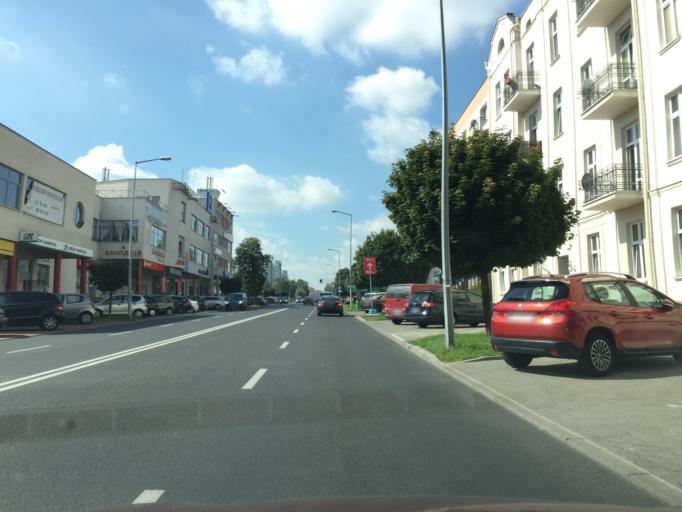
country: PL
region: Greater Poland Voivodeship
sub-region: Kalisz
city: Kalisz
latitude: 51.7513
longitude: 18.0764
